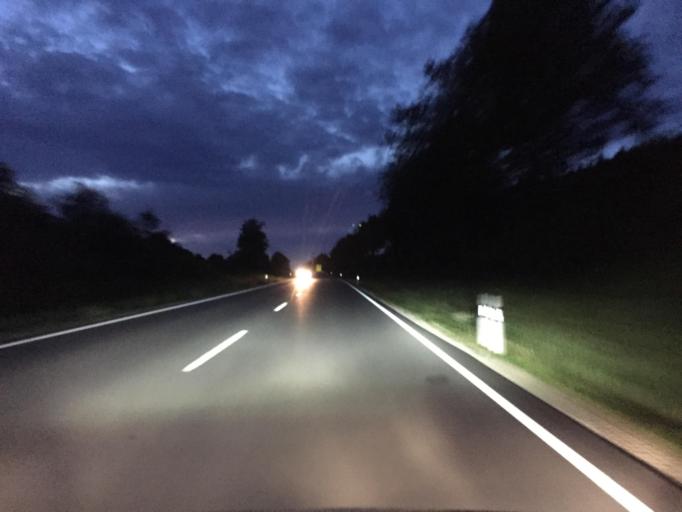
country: DE
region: Baden-Wuerttemberg
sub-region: Freiburg Region
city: Blumberg
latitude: 47.8792
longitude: 8.5343
